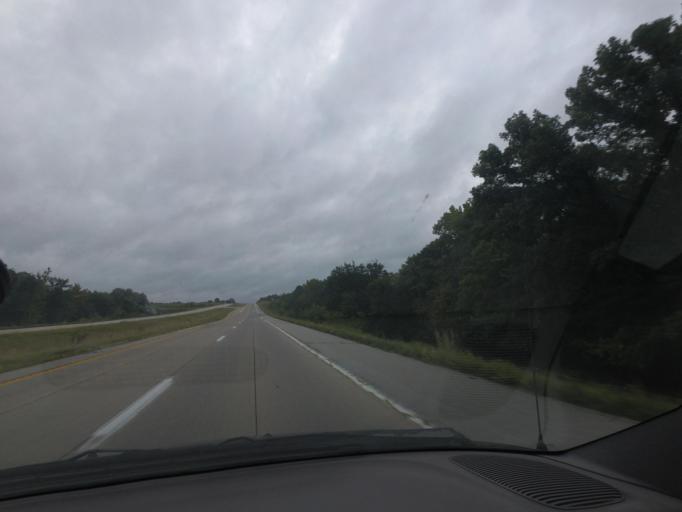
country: US
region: Missouri
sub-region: Marion County
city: Monroe City
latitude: 39.6737
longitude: -91.8871
